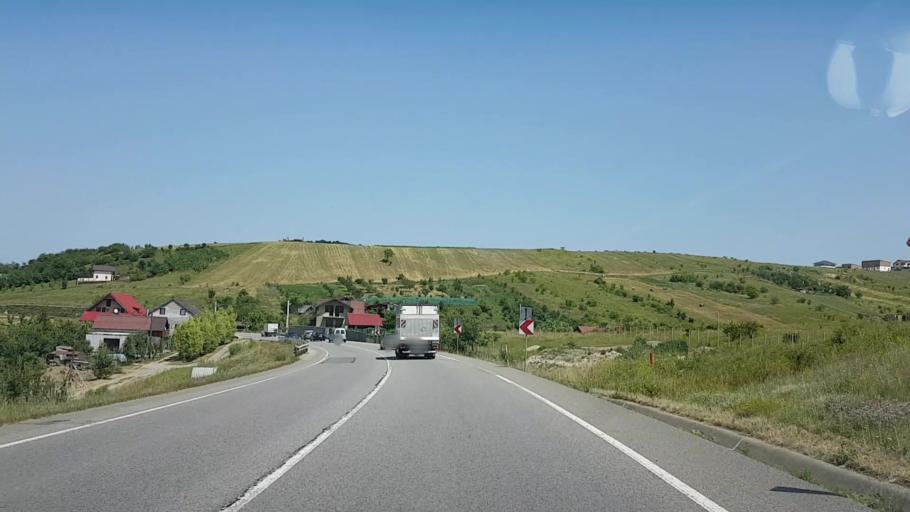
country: RO
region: Cluj
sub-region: Comuna Apahida
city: Dezmir
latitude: 46.7708
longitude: 23.6974
